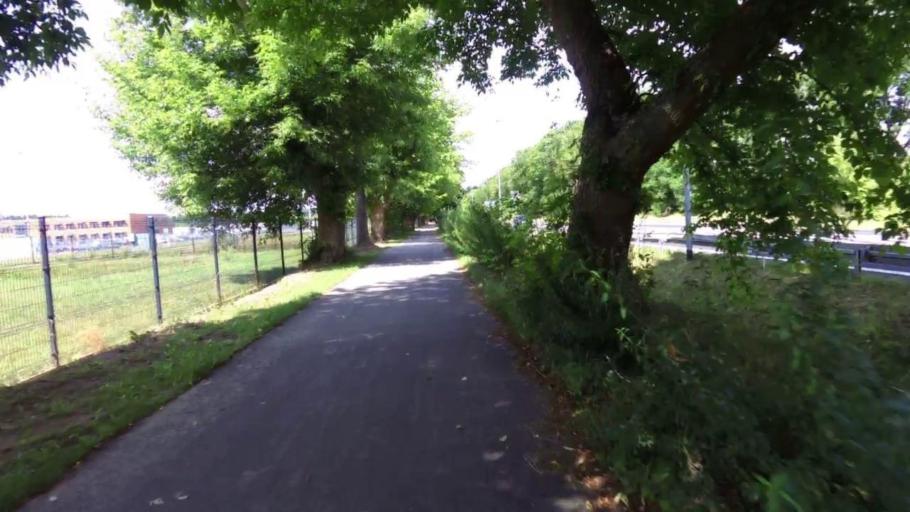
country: PL
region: West Pomeranian Voivodeship
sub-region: Powiat stargardzki
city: Kobylanka
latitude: 53.3475
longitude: 14.8468
